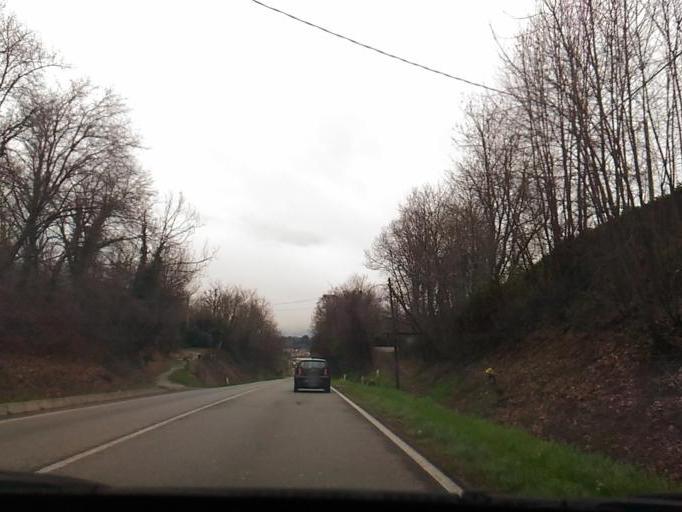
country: IT
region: Lombardy
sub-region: Provincia di Como
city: Carugo
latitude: 45.7107
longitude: 9.1785
